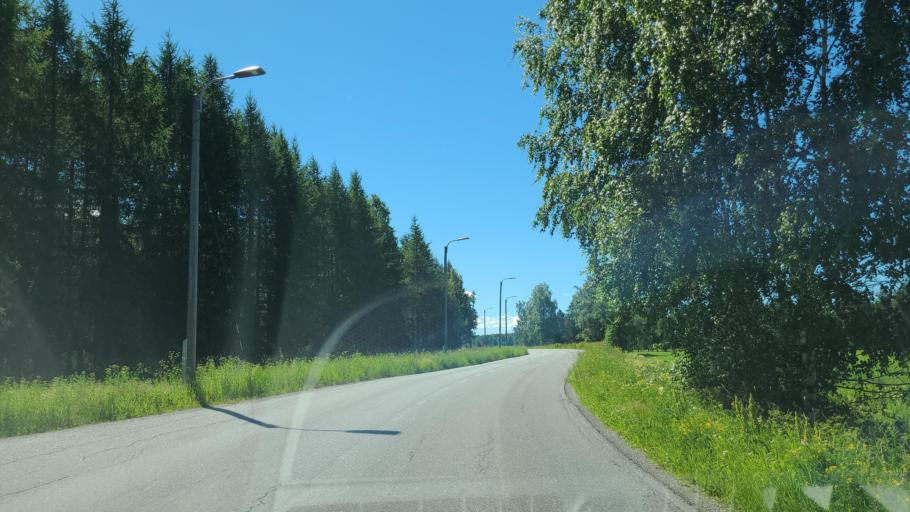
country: FI
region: Ostrobothnia
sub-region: Vaasa
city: Ristinummi
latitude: 63.0688
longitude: 21.7243
